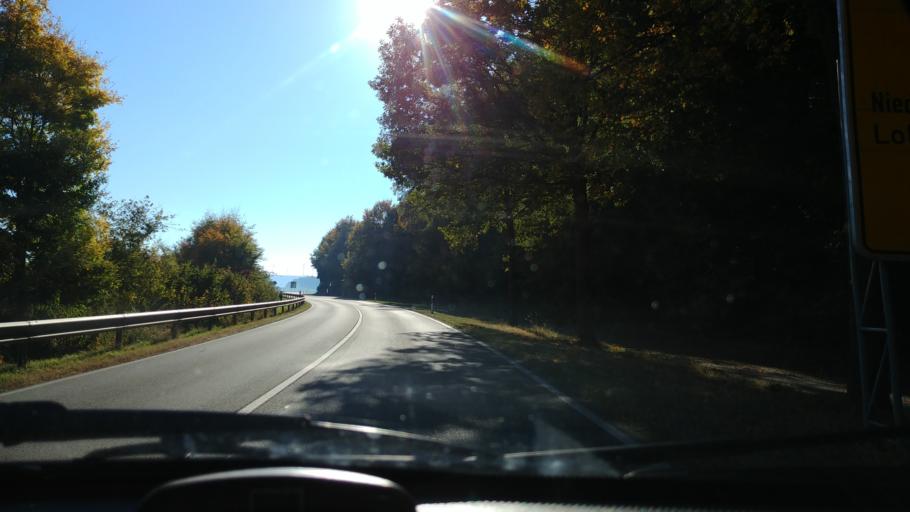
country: DE
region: Rheinland-Pfalz
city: Lollschied
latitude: 50.2581
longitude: 7.8548
